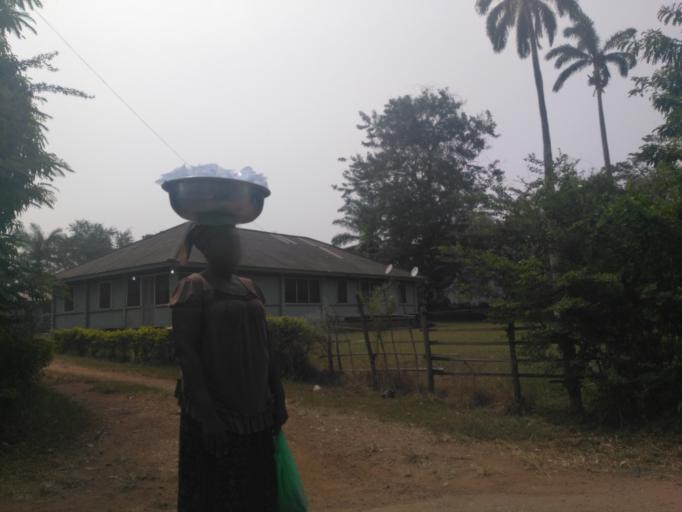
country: GH
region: Ashanti
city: Kumasi
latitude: 6.6870
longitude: -1.6306
